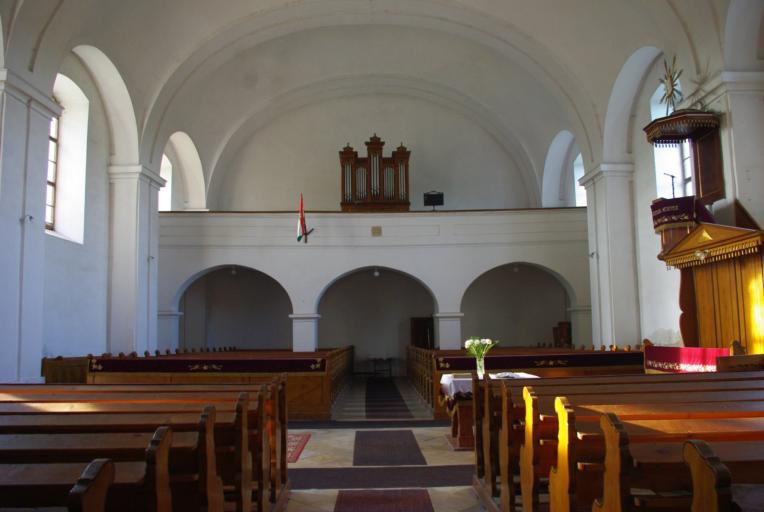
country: HU
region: Baranya
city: Sellye
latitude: 45.8750
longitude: 17.8442
